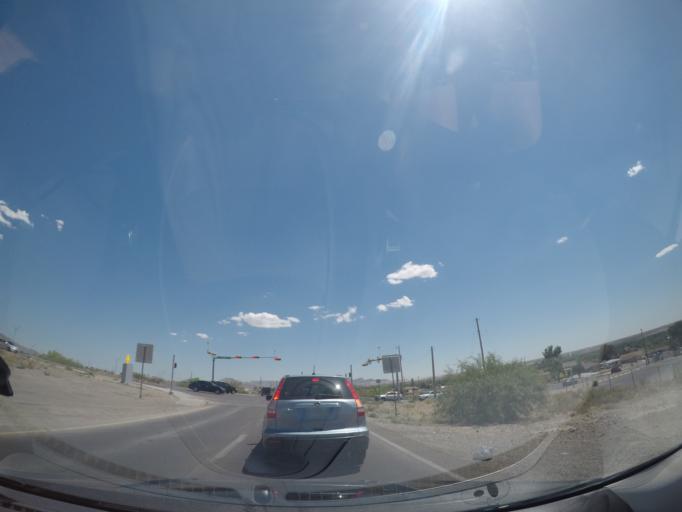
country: US
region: New Mexico
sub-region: Dona Ana County
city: Sunland Park
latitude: 31.8527
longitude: -106.5755
